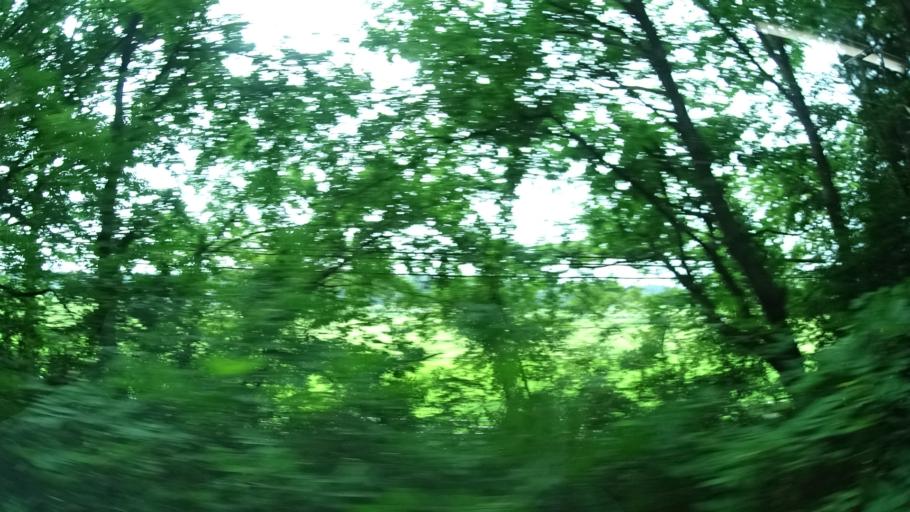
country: JP
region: Tochigi
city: Mashiko
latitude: 36.5207
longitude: 140.0909
